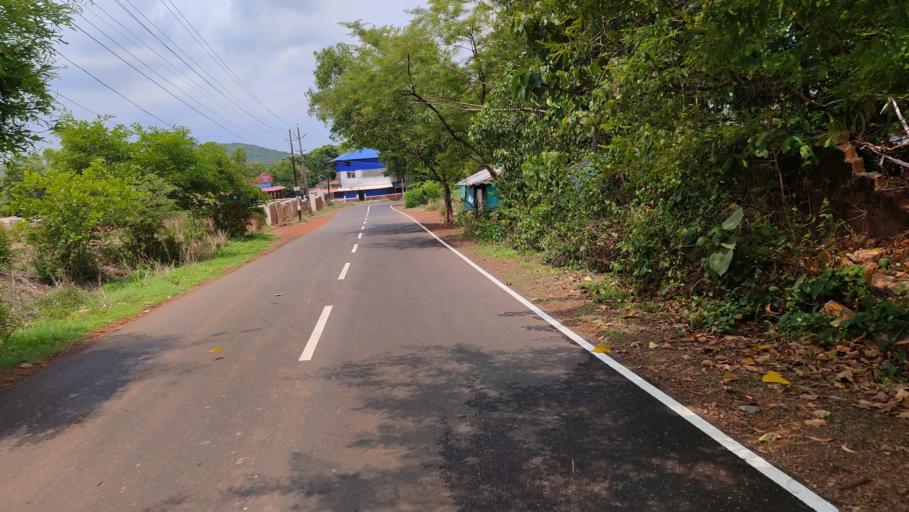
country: IN
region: Kerala
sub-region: Kasaragod District
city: Kannangad
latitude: 12.3226
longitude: 75.1323
